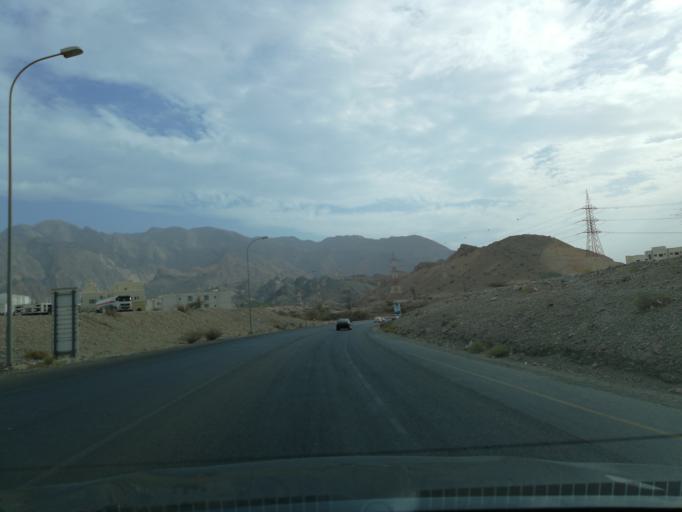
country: OM
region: Muhafazat Masqat
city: Bawshar
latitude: 23.4796
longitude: 58.3070
